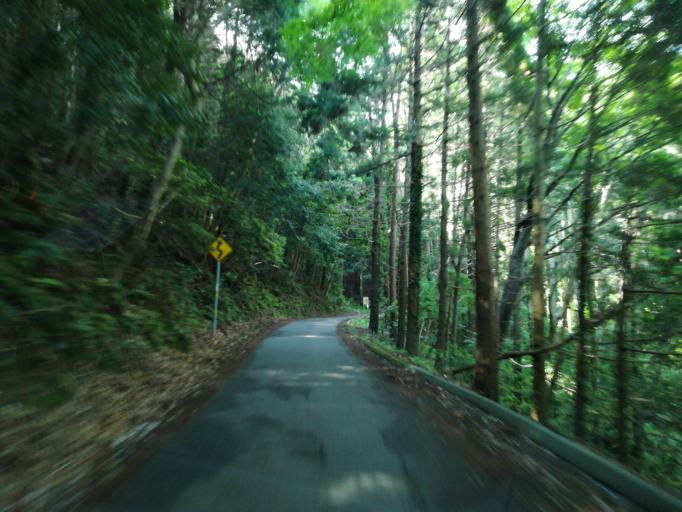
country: JP
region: Ibaraki
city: Tsukuba
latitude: 36.1844
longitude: 140.1182
